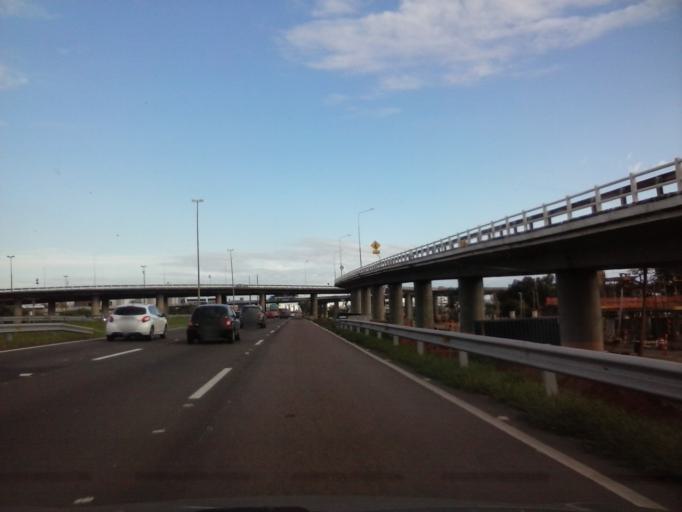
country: BR
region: Rio Grande do Sul
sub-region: Porto Alegre
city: Porto Alegre
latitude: -29.9957
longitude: -51.2059
